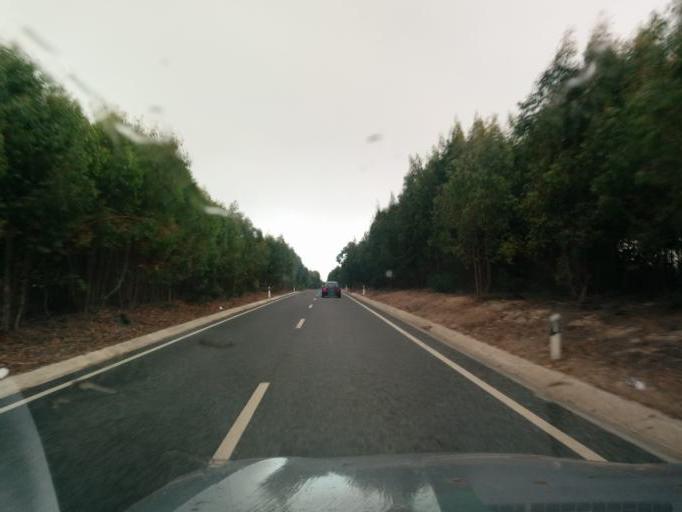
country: PT
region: Beja
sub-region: Odemira
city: Vila Nova de Milfontes
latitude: 37.6600
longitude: -8.7595
